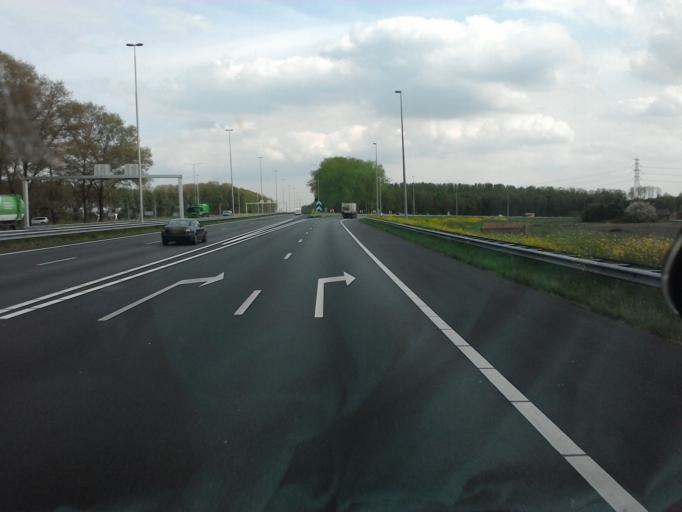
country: NL
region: Gelderland
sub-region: Gemeente Beuningen
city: Beuningen
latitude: 51.8435
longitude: 5.7740
